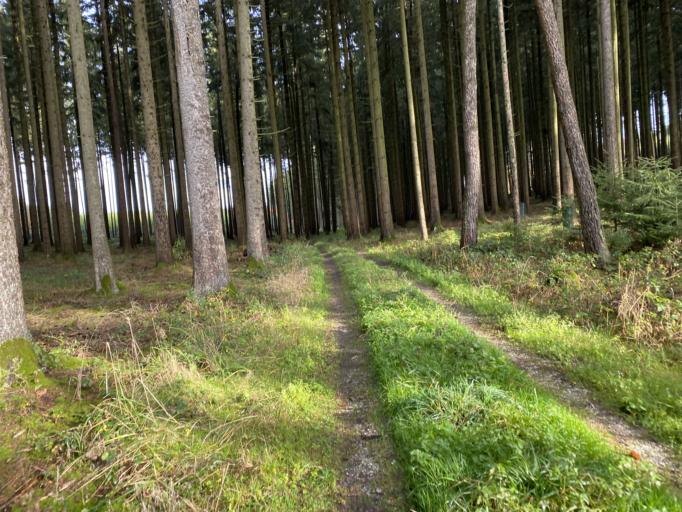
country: DE
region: Bavaria
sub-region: Upper Bavaria
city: Wolfersdorf
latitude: 48.5023
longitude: 11.7143
